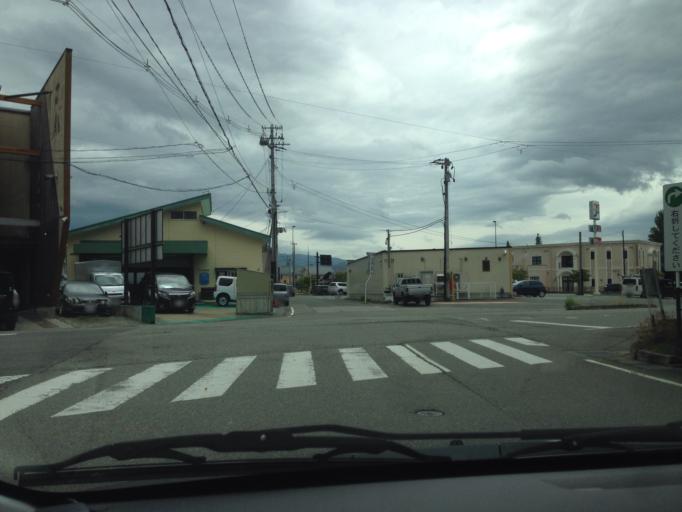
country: JP
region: Fukushima
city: Kitakata
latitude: 37.4725
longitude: 139.9046
